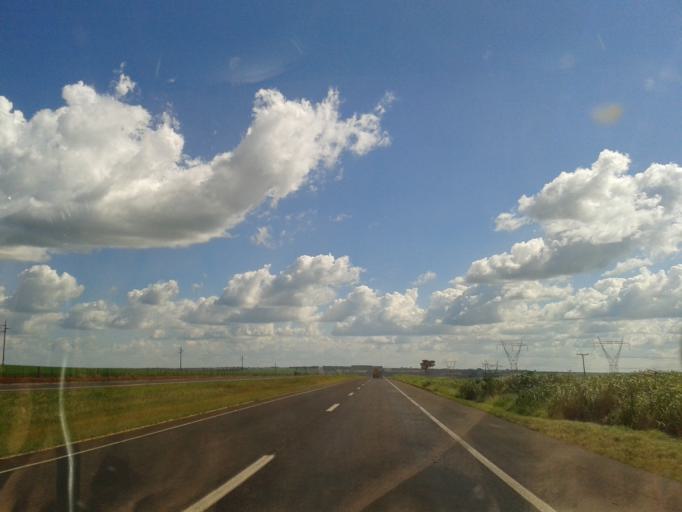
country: BR
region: Goias
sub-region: Goiatuba
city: Goiatuba
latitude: -17.9778
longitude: -49.2563
